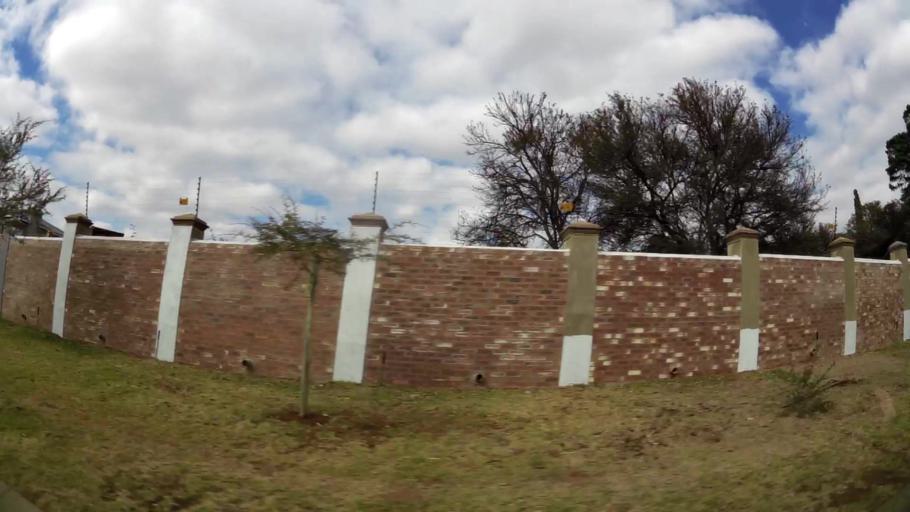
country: ZA
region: Gauteng
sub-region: West Rand District Municipality
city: Muldersdriseloop
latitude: -26.0931
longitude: 27.8579
